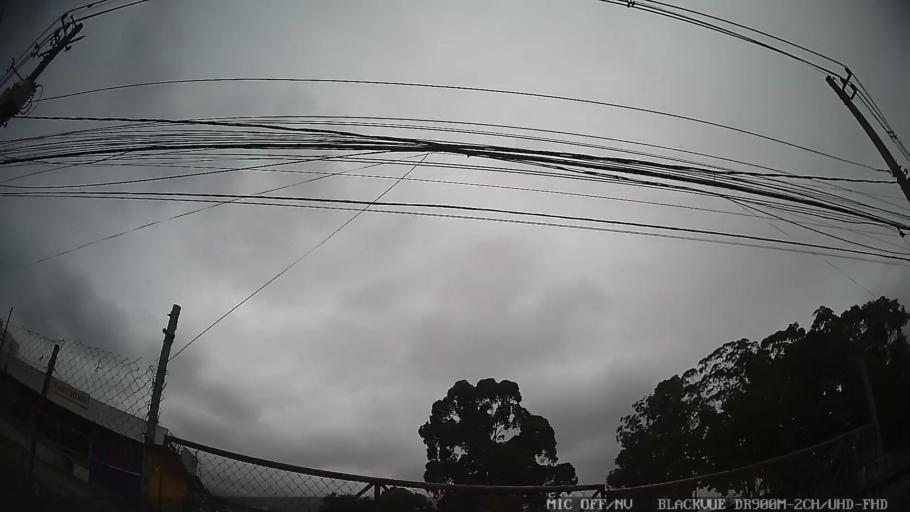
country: BR
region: Sao Paulo
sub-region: Osasco
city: Osasco
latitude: -23.4869
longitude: -46.7568
